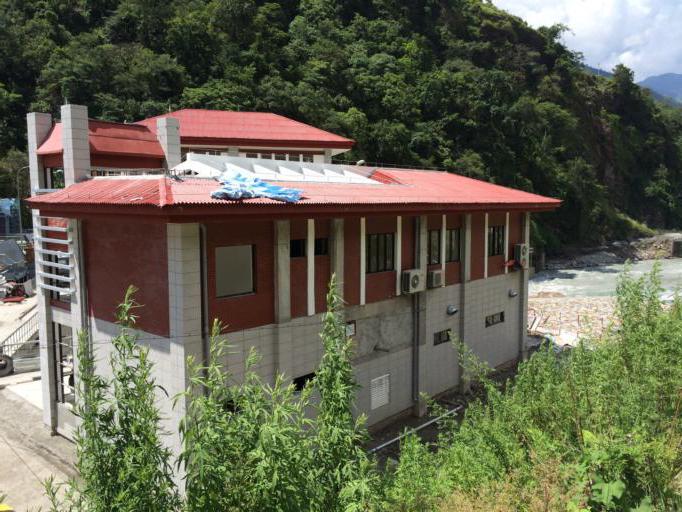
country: NP
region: Western Region
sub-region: Gandaki Zone
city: Khudi
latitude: 28.3119
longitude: 84.4010
